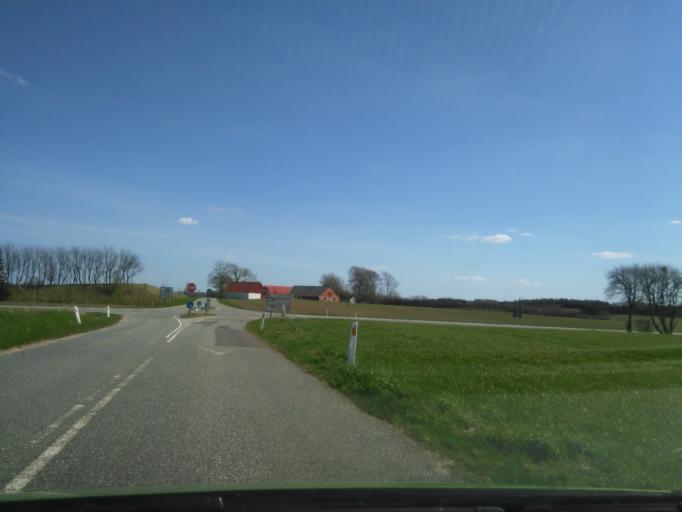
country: DK
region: Central Jutland
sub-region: Silkeborg Kommune
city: Kjellerup
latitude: 56.3469
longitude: 9.3513
